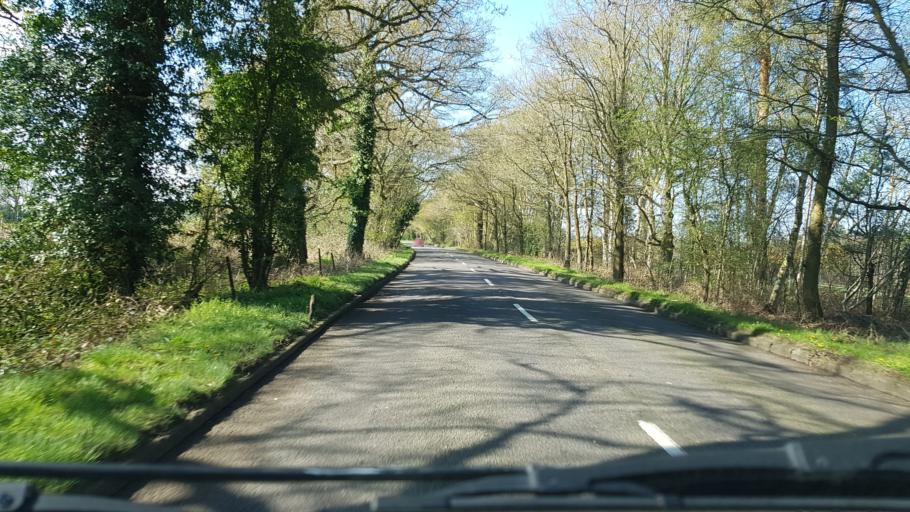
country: GB
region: England
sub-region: Surrey
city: Normandy
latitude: 51.2671
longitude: -0.6670
